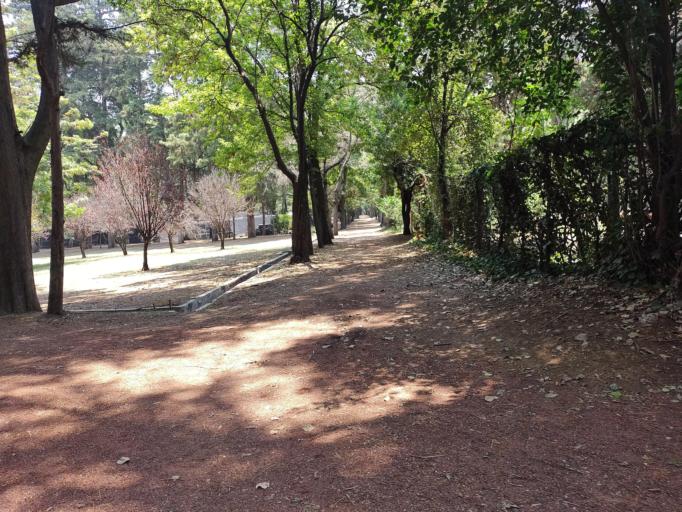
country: MX
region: Mexico City
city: Coyoacan
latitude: 19.3536
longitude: -99.1737
